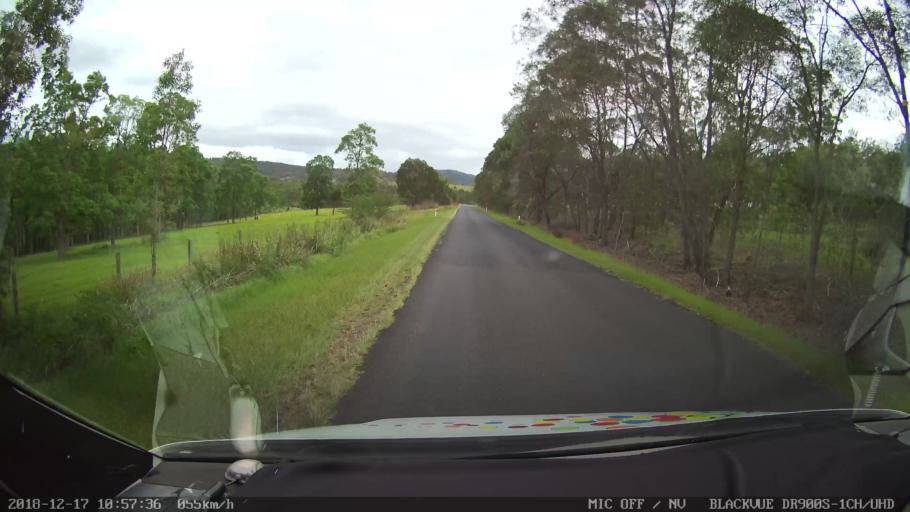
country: AU
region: New South Wales
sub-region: Richmond Valley
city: Casino
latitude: -28.8243
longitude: 152.5984
